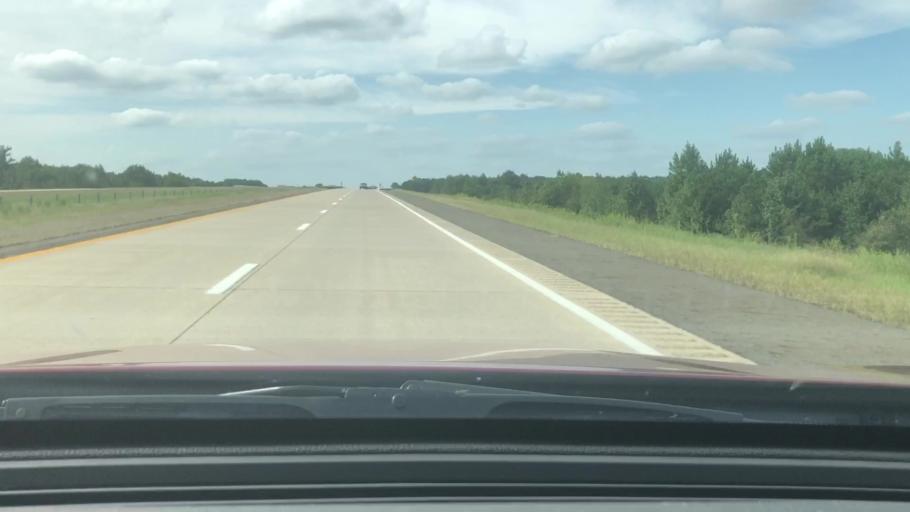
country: US
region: Texas
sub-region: Bowie County
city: Texarkana
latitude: 33.2488
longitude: -93.8833
